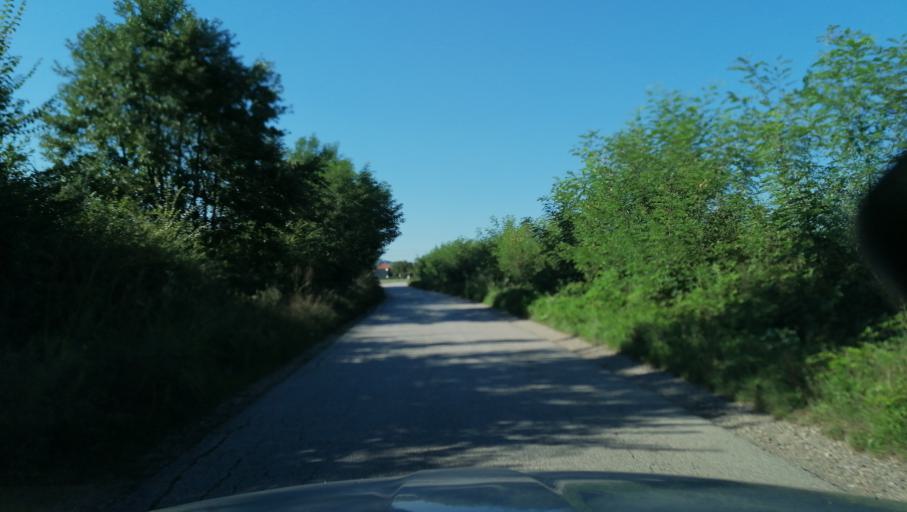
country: RS
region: Central Serbia
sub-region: Sumadijski Okrug
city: Knic
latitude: 43.8912
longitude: 20.6156
